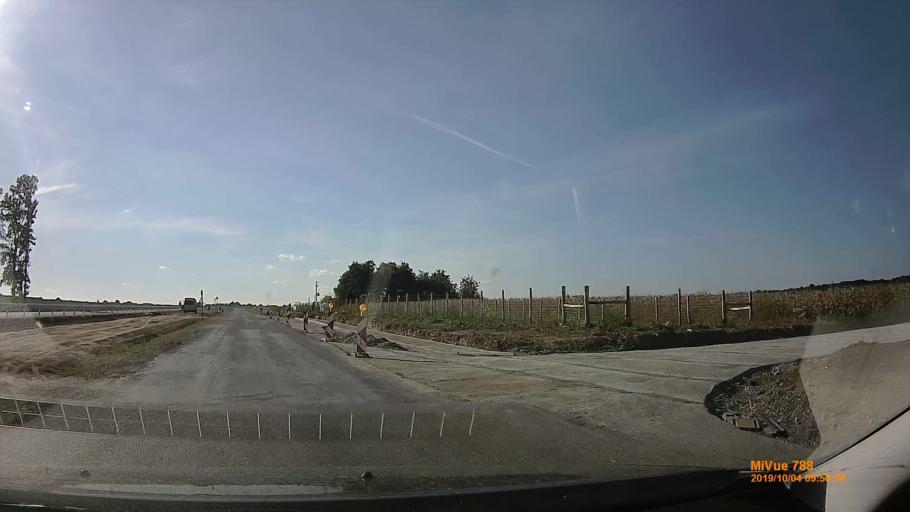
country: HU
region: Somogy
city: Kaposvar
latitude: 46.4376
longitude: 17.7707
